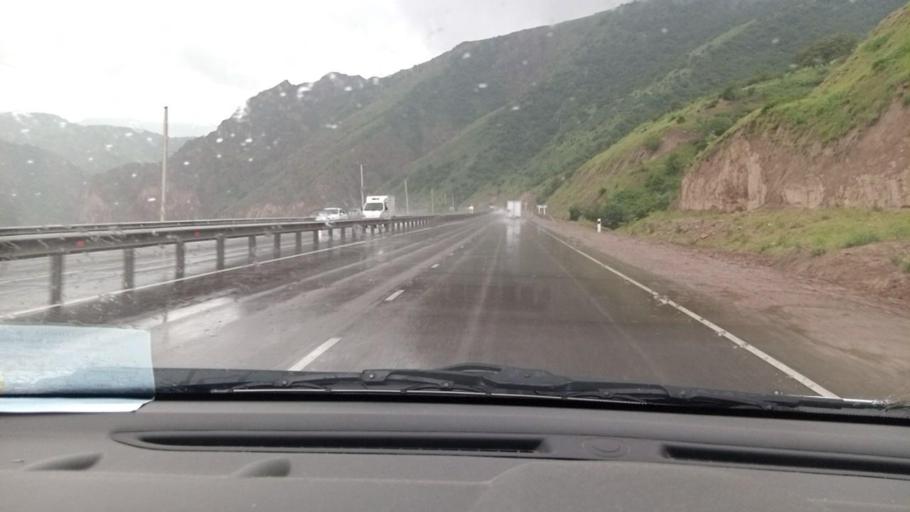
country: UZ
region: Toshkent
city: Angren
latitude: 41.0959
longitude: 70.3215
